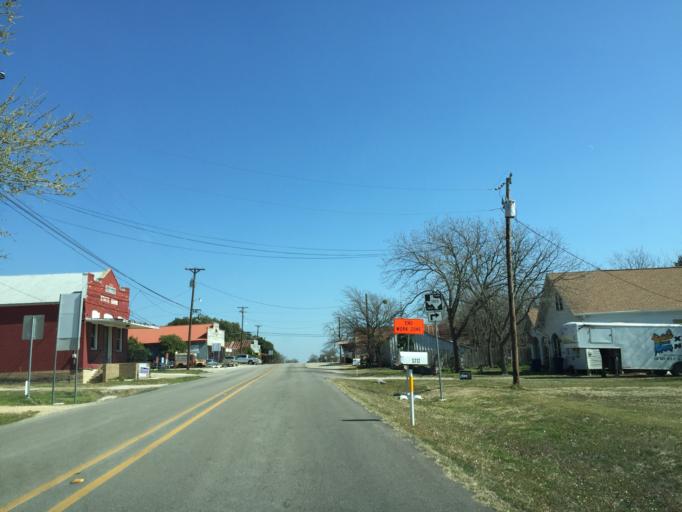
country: US
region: Texas
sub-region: Williamson County
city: Serenada
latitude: 30.7344
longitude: -97.5887
